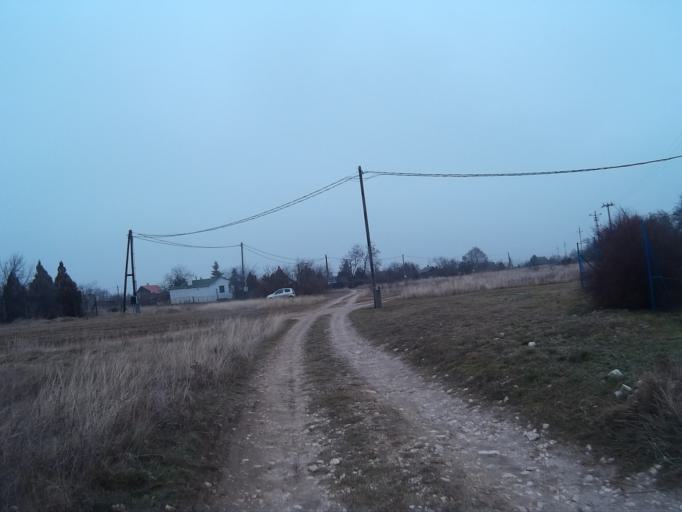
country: HU
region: Fejer
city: Csakvar
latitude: 47.3819
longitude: 18.4440
